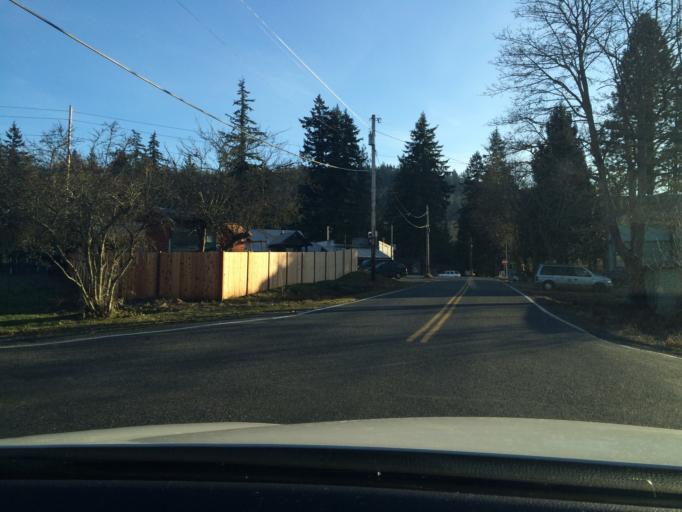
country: US
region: Washington
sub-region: Whatcom County
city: Geneva
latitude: 48.8042
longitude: -122.3989
